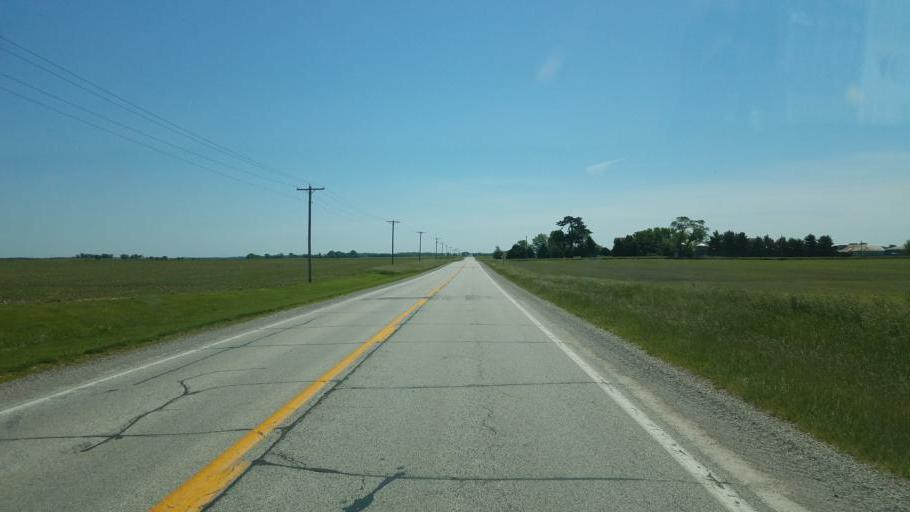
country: US
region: Illinois
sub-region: McLean County
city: Heyworth
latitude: 40.3120
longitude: -89.0633
